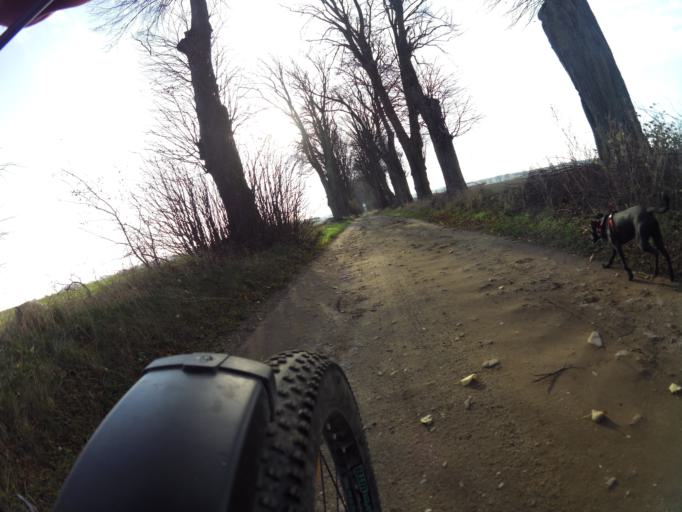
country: PL
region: Pomeranian Voivodeship
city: Strzelno
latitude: 54.7553
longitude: 18.2913
